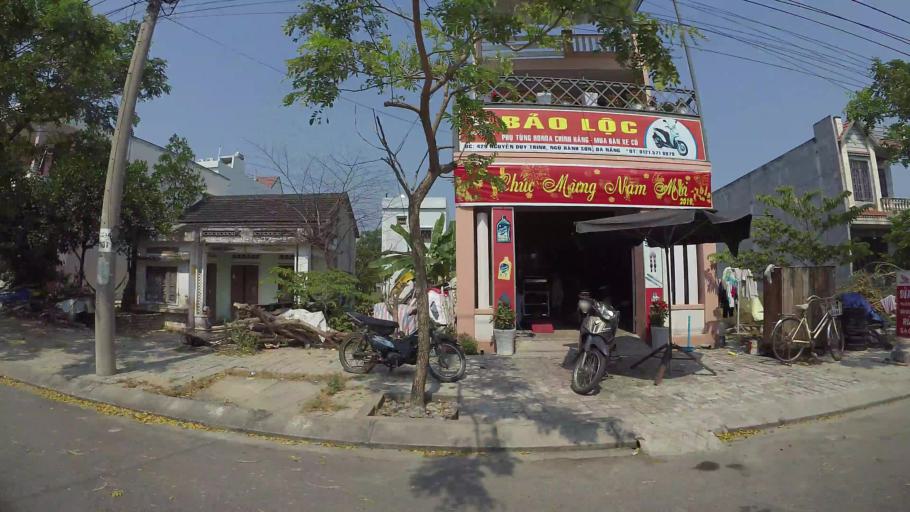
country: VN
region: Da Nang
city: Ngu Hanh Son
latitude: 15.9833
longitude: 108.2723
